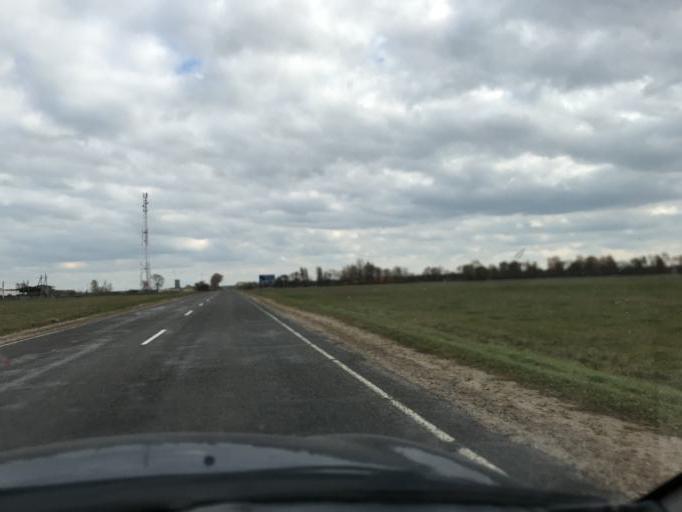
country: BY
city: Berezovka
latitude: 53.7403
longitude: 25.3658
